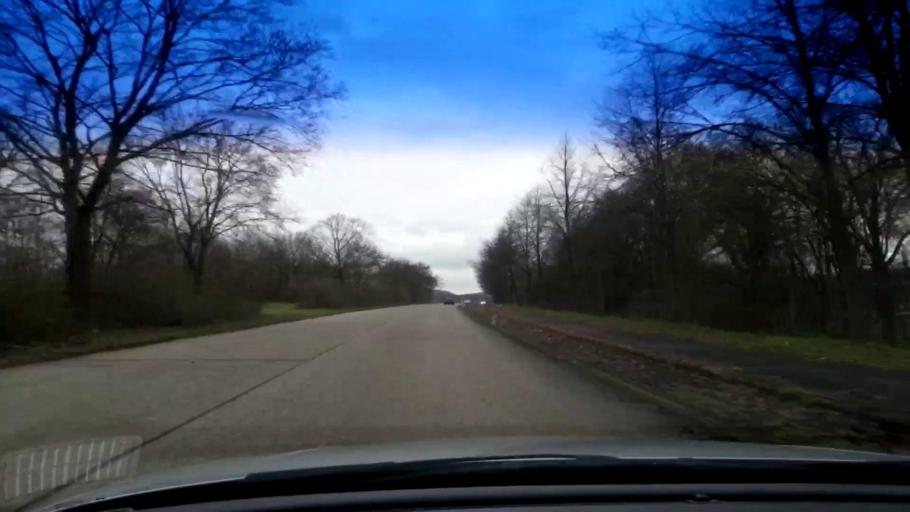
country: DE
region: Bavaria
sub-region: Upper Franconia
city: Bamberg
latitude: 49.8777
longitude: 10.9085
